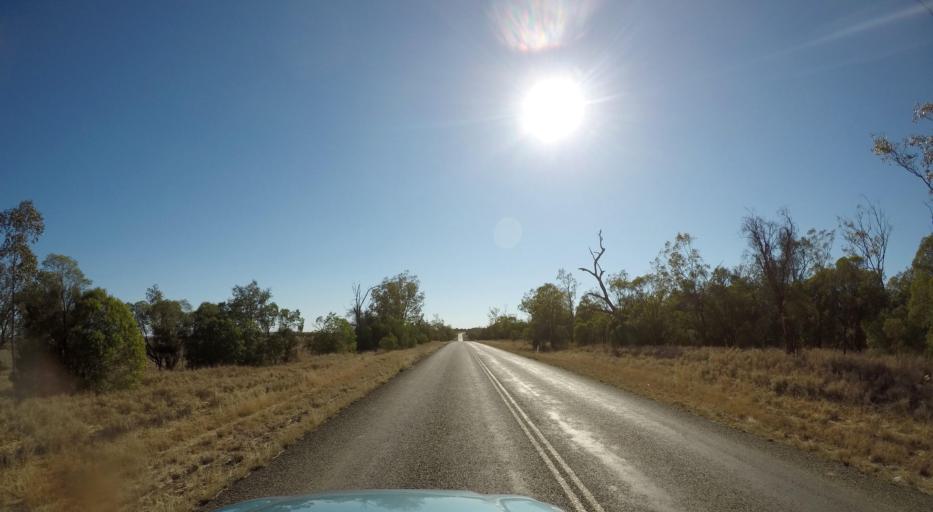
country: AU
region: Queensland
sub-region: Banana
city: Taroom
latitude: -26.0012
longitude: 149.3533
